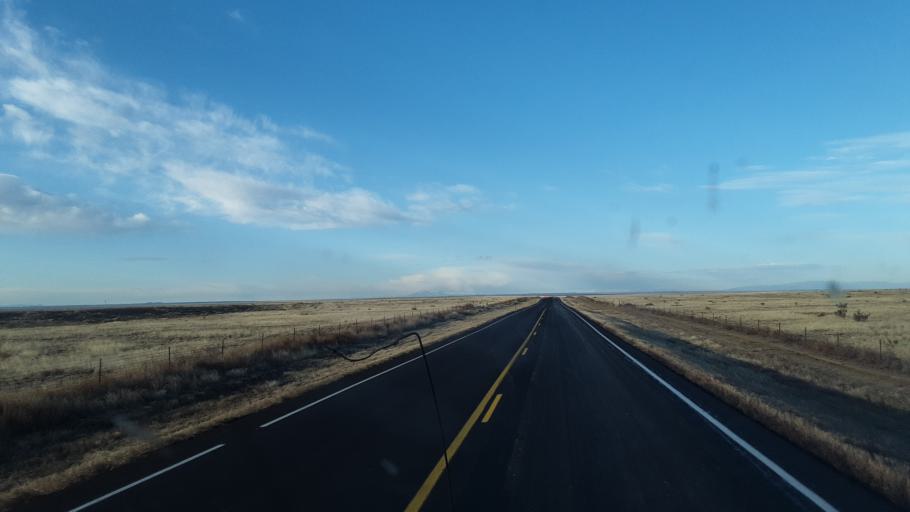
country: US
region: Colorado
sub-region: Otero County
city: Rocky Ford
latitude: 37.9695
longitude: -103.8224
